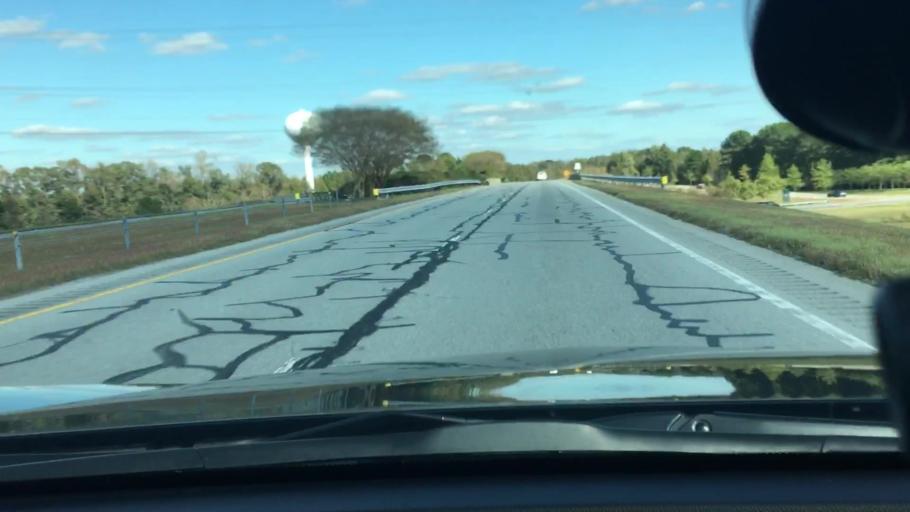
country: US
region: North Carolina
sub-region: Pitt County
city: Farmville
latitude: 35.6181
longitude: -77.6070
